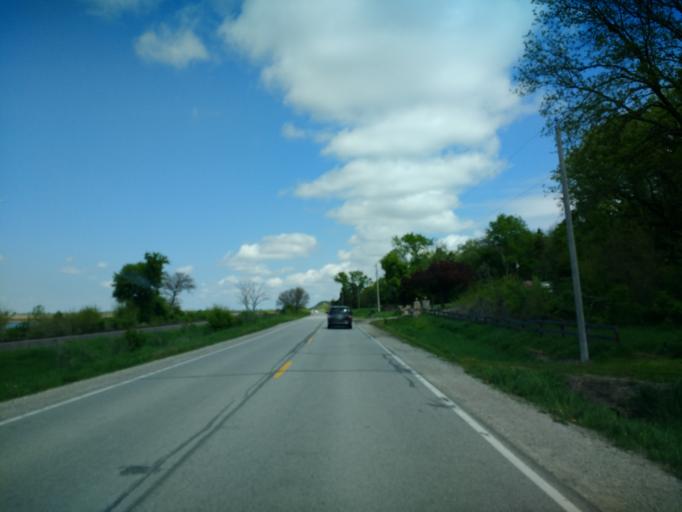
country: US
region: Iowa
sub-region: Harrison County
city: Missouri Valley
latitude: 41.4458
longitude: -95.8711
